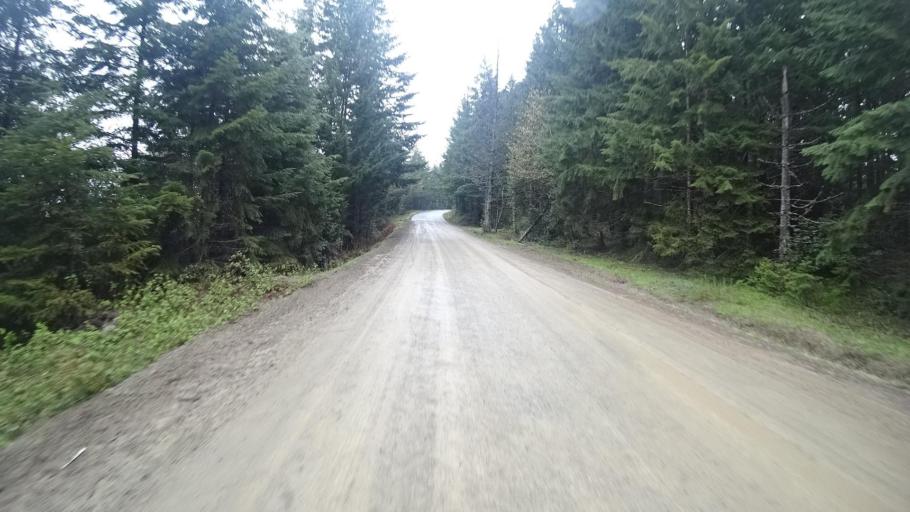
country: US
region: California
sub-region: Humboldt County
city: Westhaven-Moonstone
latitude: 41.1404
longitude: -123.8583
